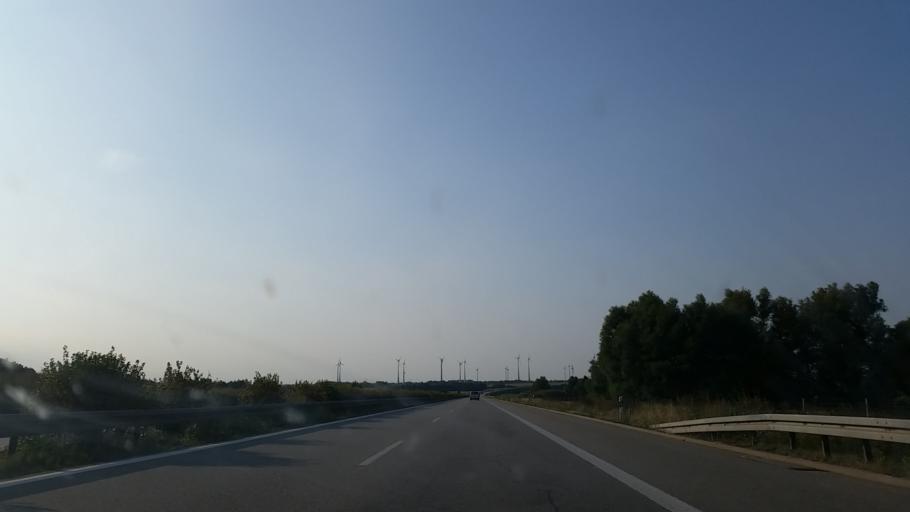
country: DE
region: Mecklenburg-Vorpommern
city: Brunn
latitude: 53.6679
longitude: 13.3471
